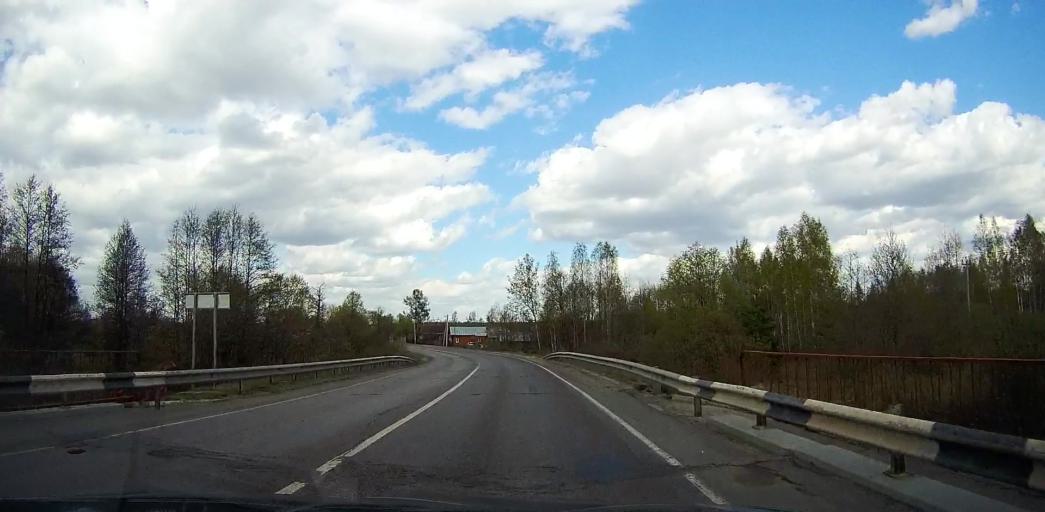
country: RU
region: Moskovskaya
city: Davydovo
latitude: 55.6324
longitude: 38.8682
